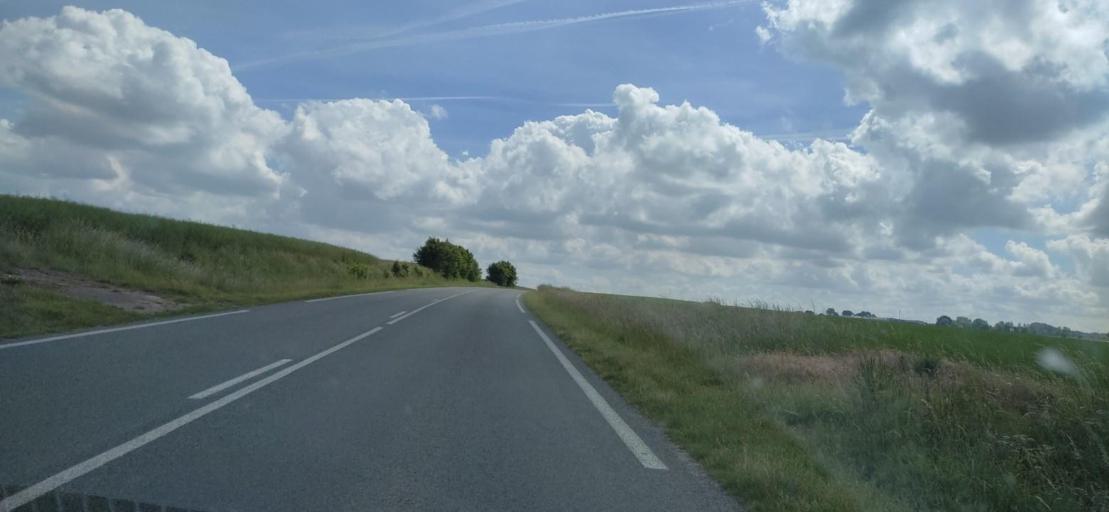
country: FR
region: Nord-Pas-de-Calais
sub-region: Departement du Pas-de-Calais
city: Therouanne
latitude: 50.6587
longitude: 2.2590
